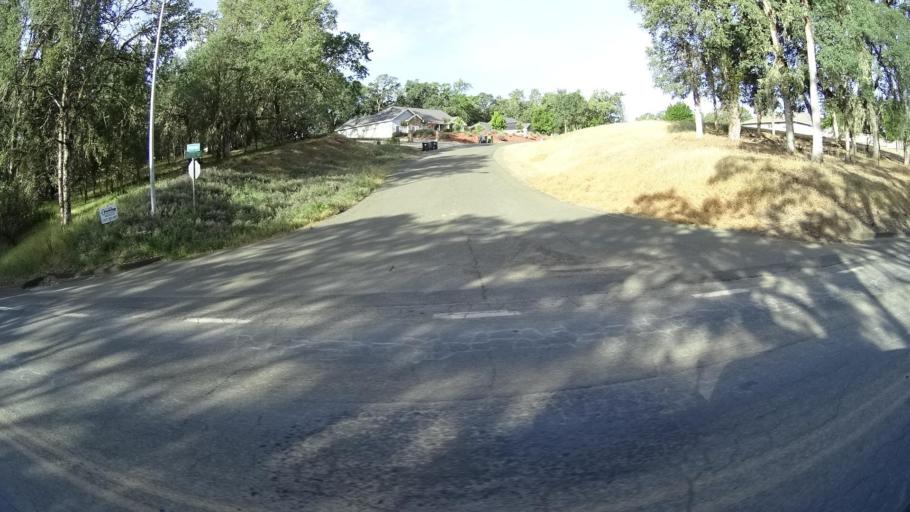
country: US
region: California
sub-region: Lake County
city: North Lakeport
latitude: 39.0806
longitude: -122.9213
